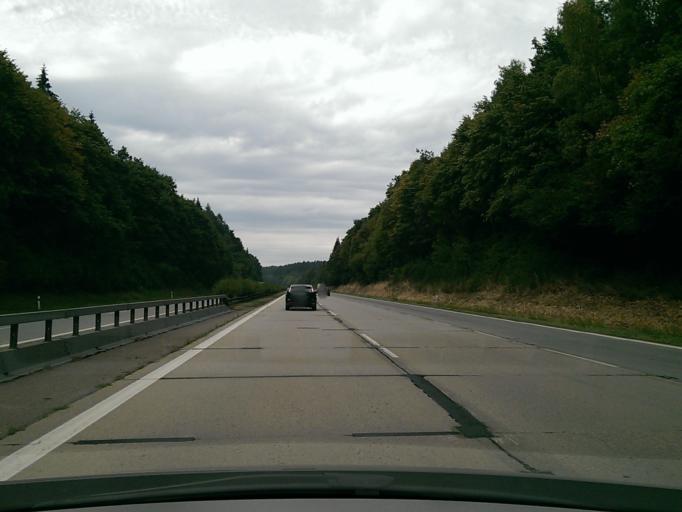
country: CZ
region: Vysocina
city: Kamenice
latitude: 49.4062
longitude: 15.8167
